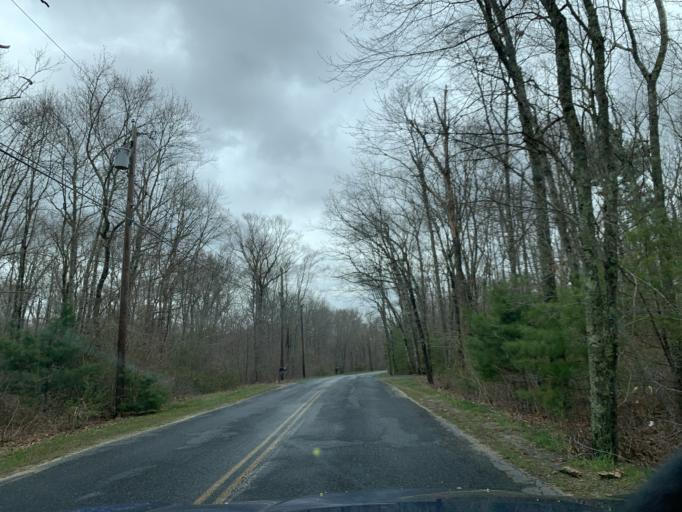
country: US
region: Massachusetts
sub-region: Bristol County
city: Rehoboth
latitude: 41.8777
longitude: -71.2094
